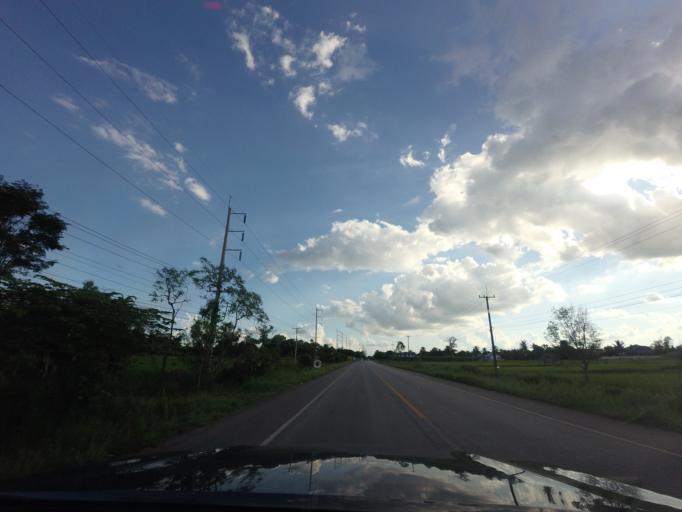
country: TH
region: Changwat Udon Thani
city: Thung Fon
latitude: 17.4597
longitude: 103.1889
